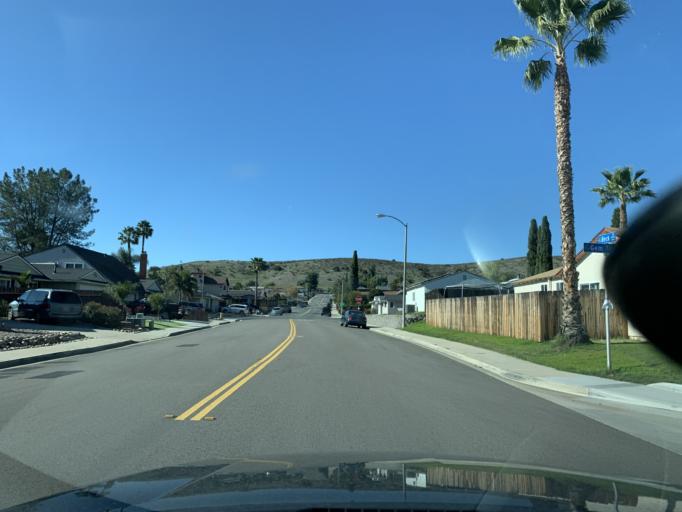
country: US
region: California
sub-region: San Diego County
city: Santee
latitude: 32.8592
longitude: -116.9783
